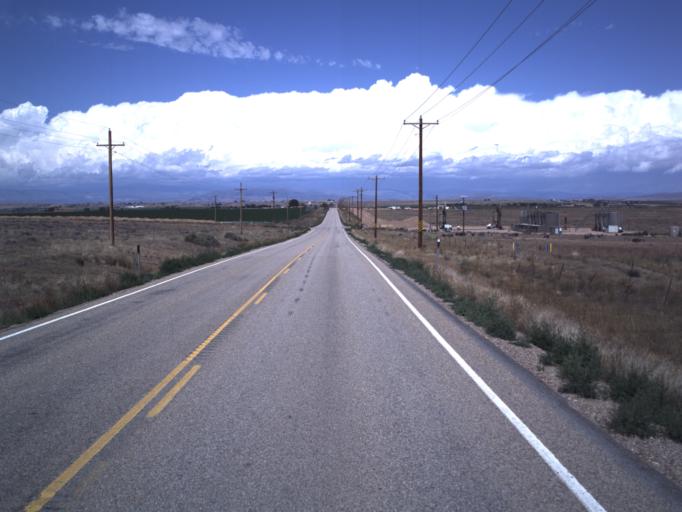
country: US
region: Utah
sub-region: Uintah County
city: Naples
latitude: 40.1566
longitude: -109.6642
